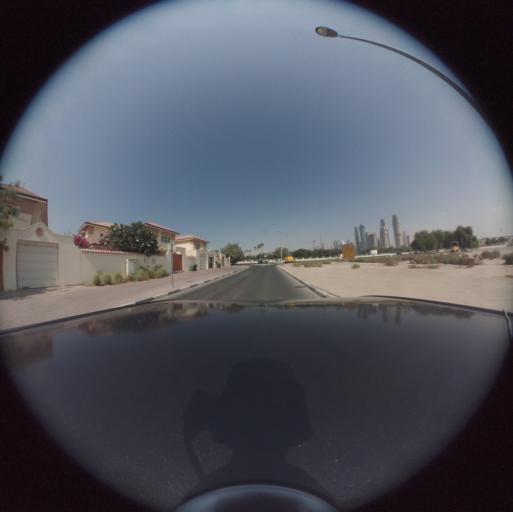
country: AE
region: Dubai
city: Dubai
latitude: 25.1826
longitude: 55.2424
